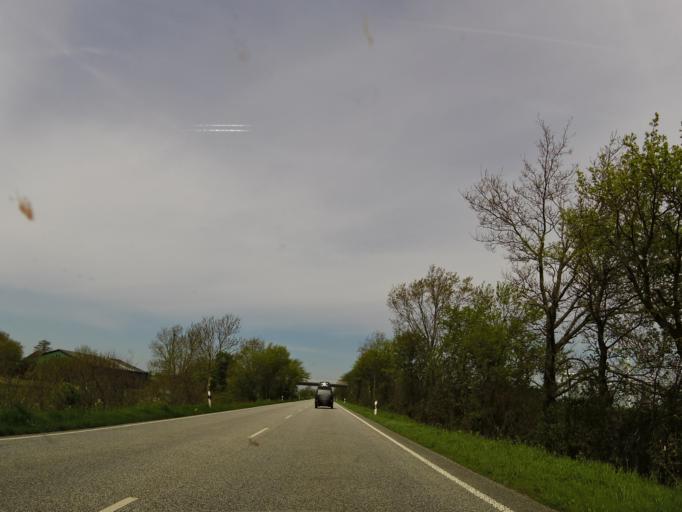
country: DE
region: Schleswig-Holstein
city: Hemme
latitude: 54.2820
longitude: 8.9977
